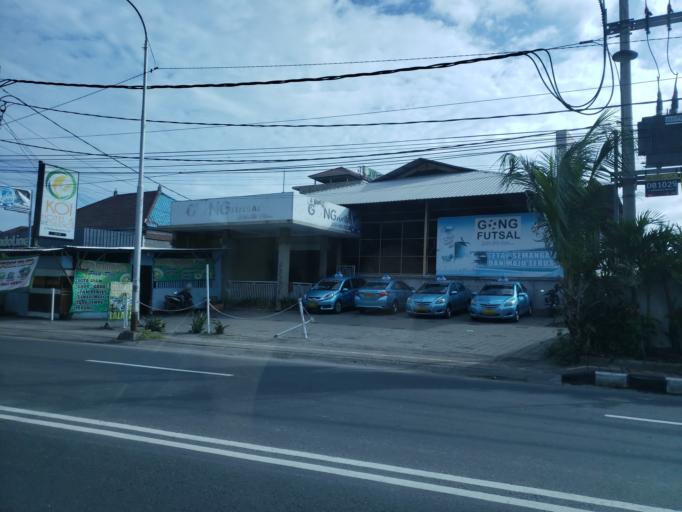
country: ID
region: Bali
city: Denpasar
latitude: -8.6769
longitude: 115.1906
